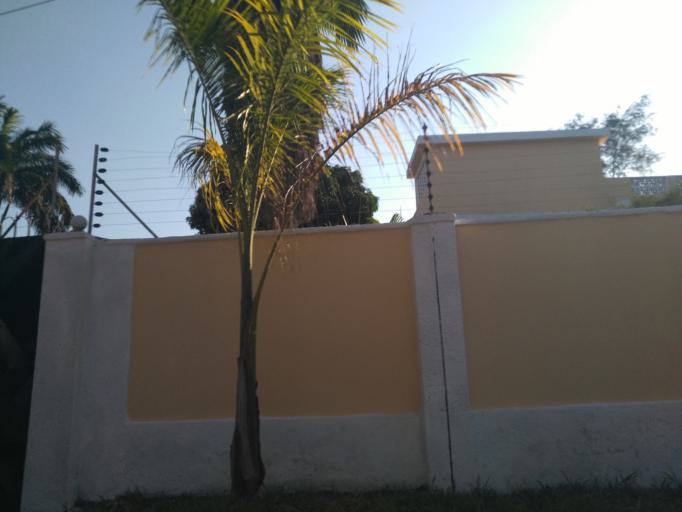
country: TZ
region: Dar es Salaam
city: Magomeni
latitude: -6.7661
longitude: 39.2561
